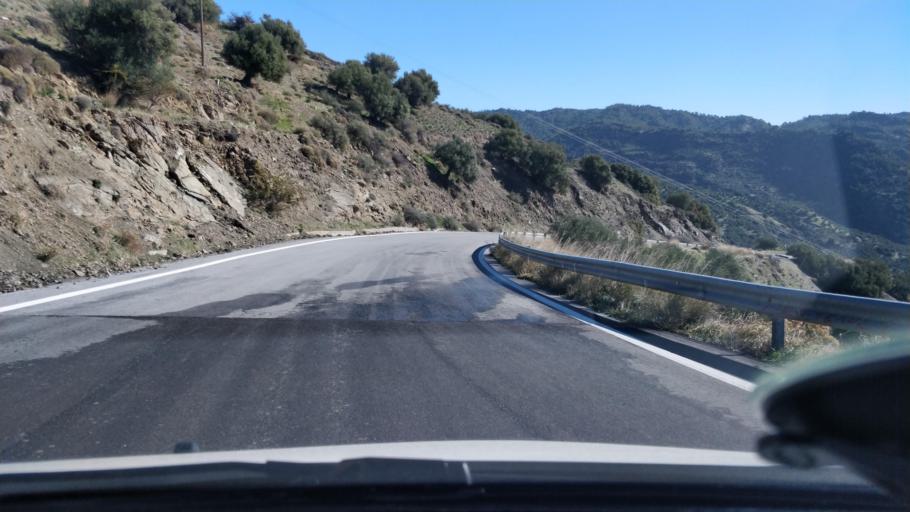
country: GR
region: Crete
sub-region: Nomos Irakleiou
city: Kastelli
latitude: 35.0340
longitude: 25.4444
